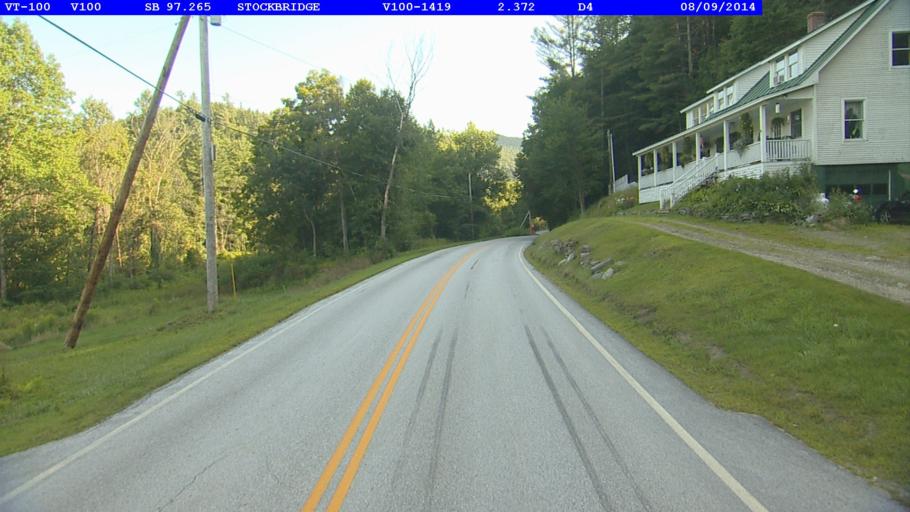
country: US
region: Vermont
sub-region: Orange County
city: Randolph
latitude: 43.7775
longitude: -72.7569
